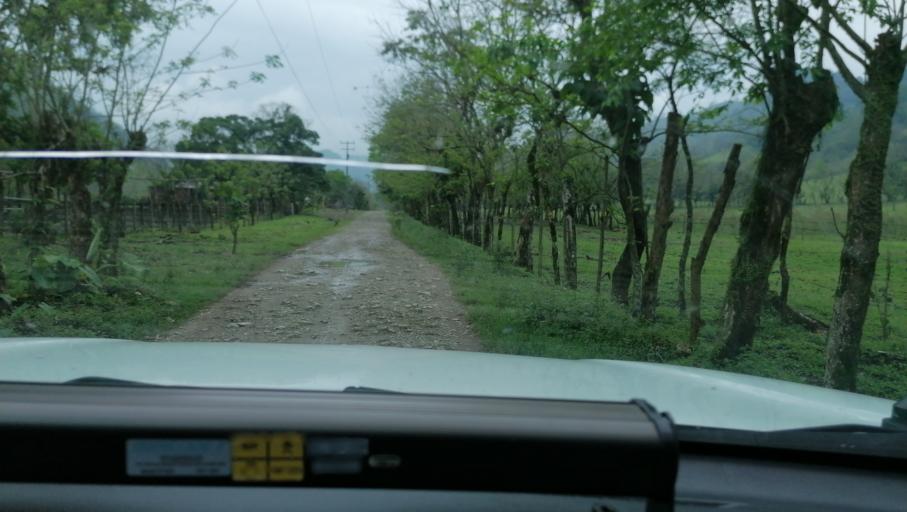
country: MX
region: Chiapas
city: Ixtacomitan
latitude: 17.3622
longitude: -93.1721
